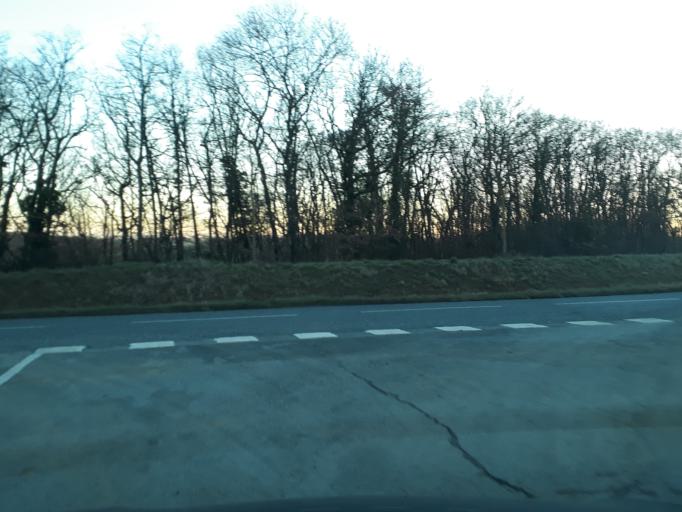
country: FR
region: Midi-Pyrenees
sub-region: Departement du Gers
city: Pavie
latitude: 43.6085
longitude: 0.6839
